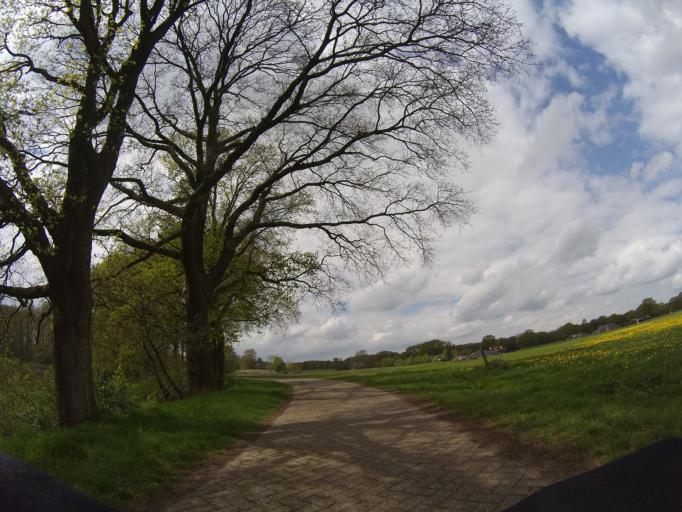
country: NL
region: Overijssel
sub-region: Gemeente Hardenberg
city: Hardenberg
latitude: 52.5544
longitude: 6.5949
